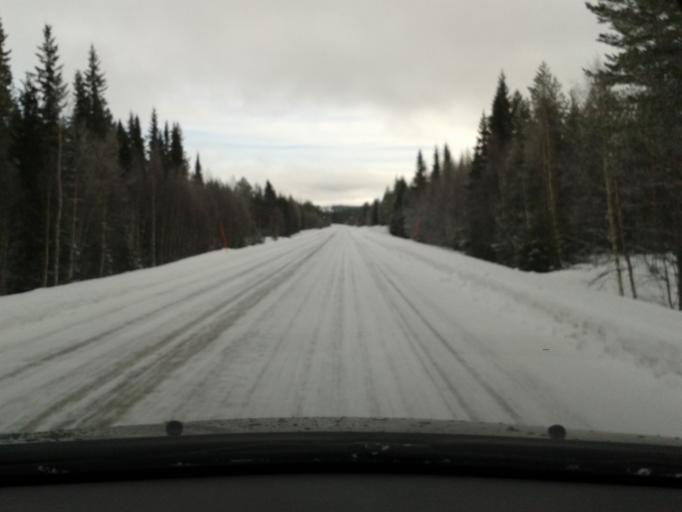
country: SE
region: Vaesterbotten
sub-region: Vilhelmina Kommun
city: Sjoberg
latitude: 64.8060
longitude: 15.9903
